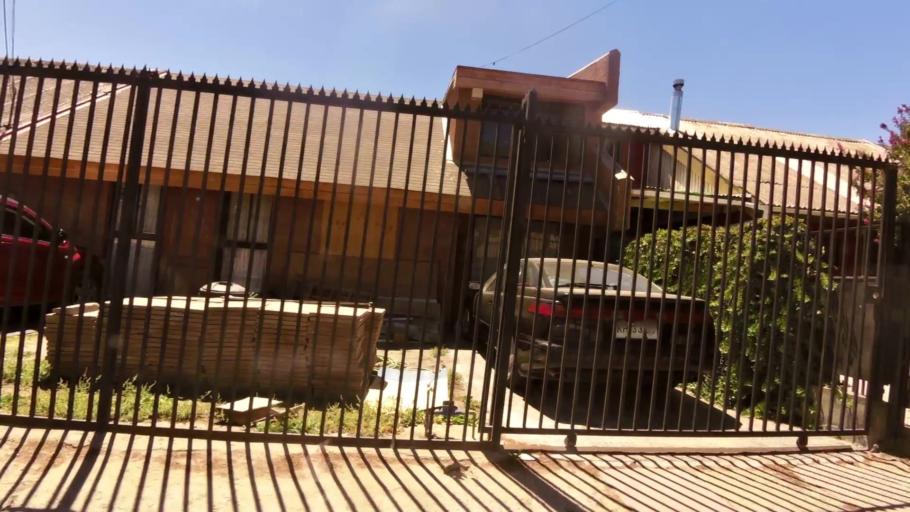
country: CL
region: O'Higgins
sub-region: Provincia de Cachapoal
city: Rancagua
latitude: -34.1586
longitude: -70.7051
